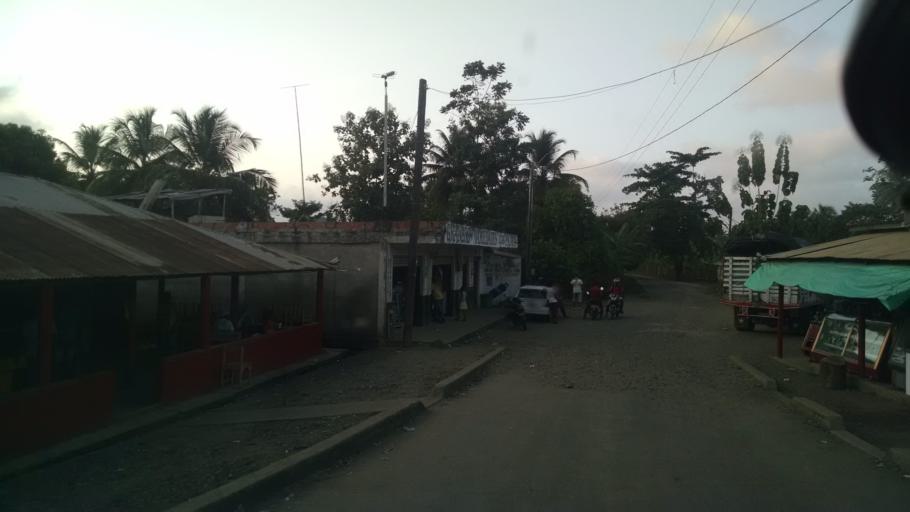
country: CO
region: Antioquia
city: San Juan de Uraba
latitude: 8.7181
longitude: -76.5986
